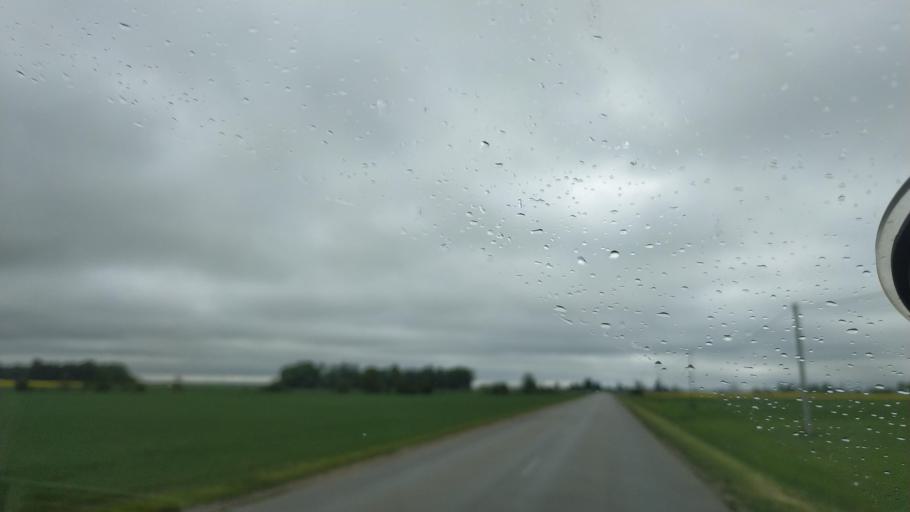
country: LT
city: Vabalninkas
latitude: 55.9937
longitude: 24.6839
